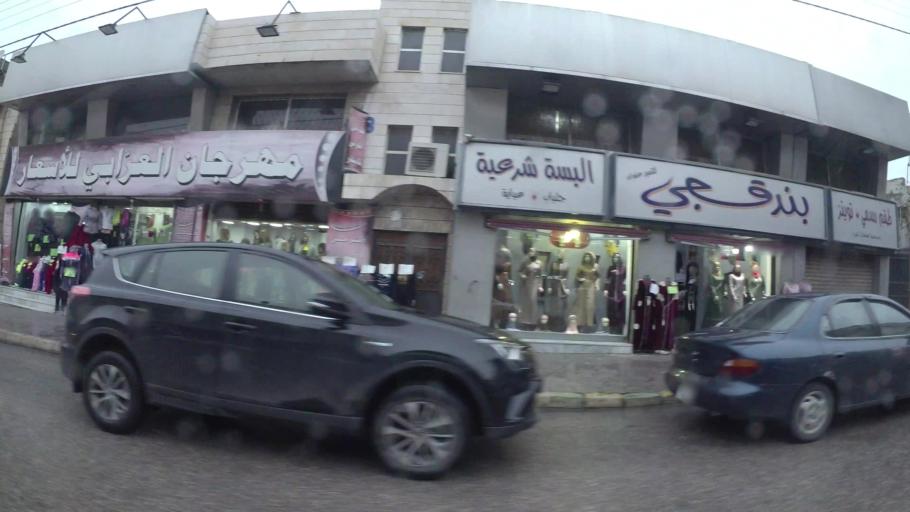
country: JO
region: Amman
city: Al Jubayhah
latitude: 32.0240
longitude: 35.8390
